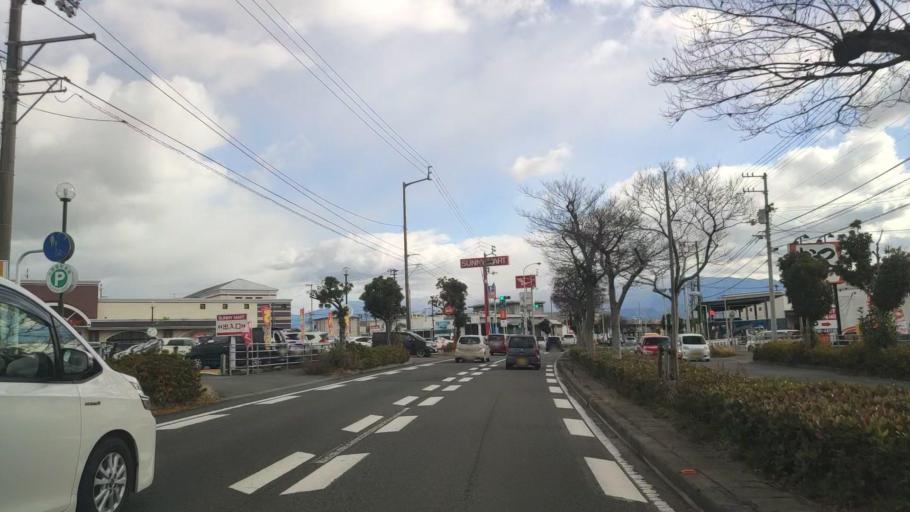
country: JP
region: Ehime
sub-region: Shikoku-chuo Shi
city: Matsuyama
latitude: 33.8186
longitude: 132.7923
